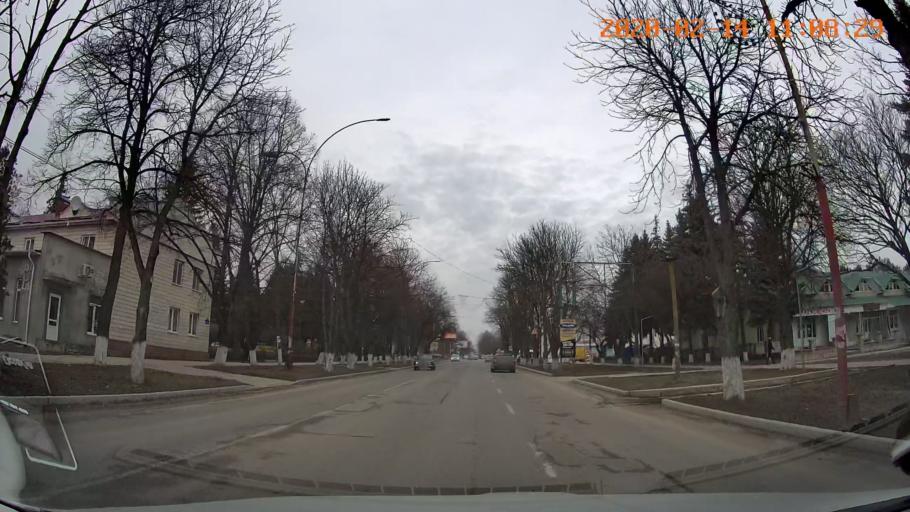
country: MD
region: Raionul Edinet
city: Edinet
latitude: 48.1723
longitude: 27.3018
